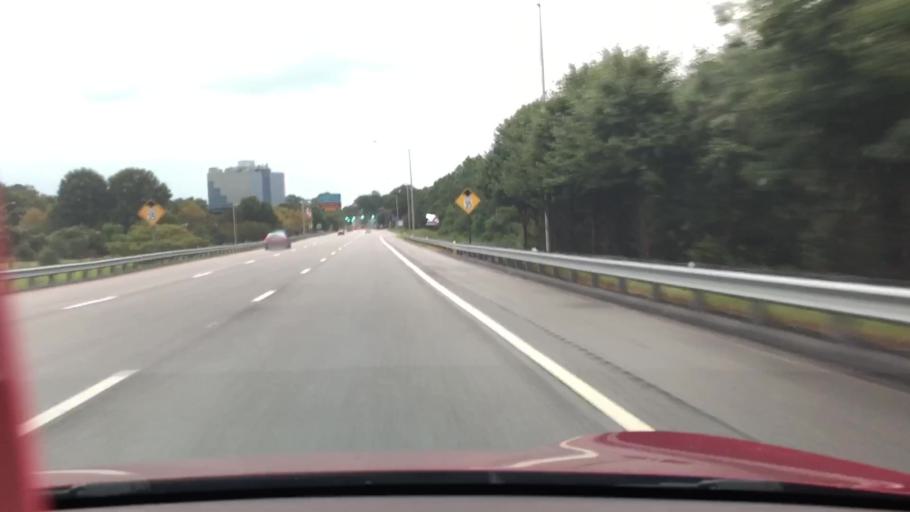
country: US
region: Virginia
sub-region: City of Virginia Beach
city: Virginia Beach
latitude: 36.8469
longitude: -75.9902
